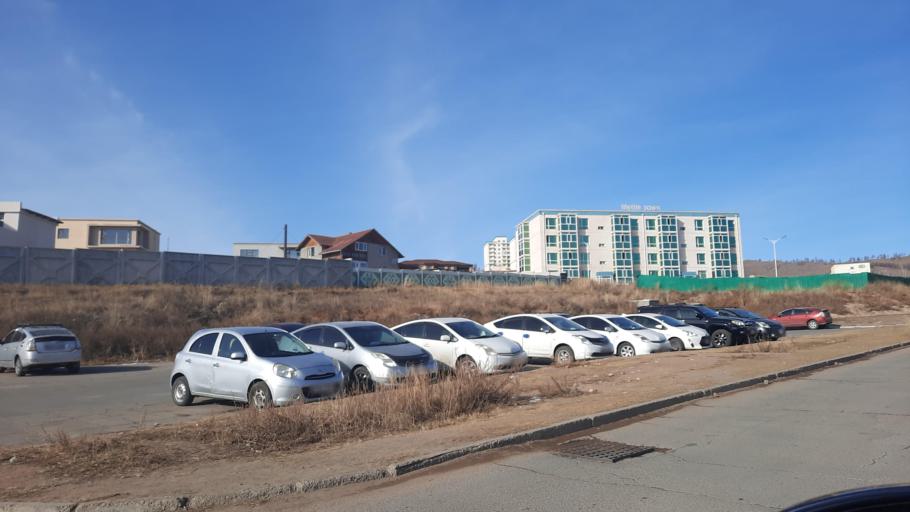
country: MN
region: Orhon
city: Erdenet
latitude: 49.0367
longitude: 104.0516
